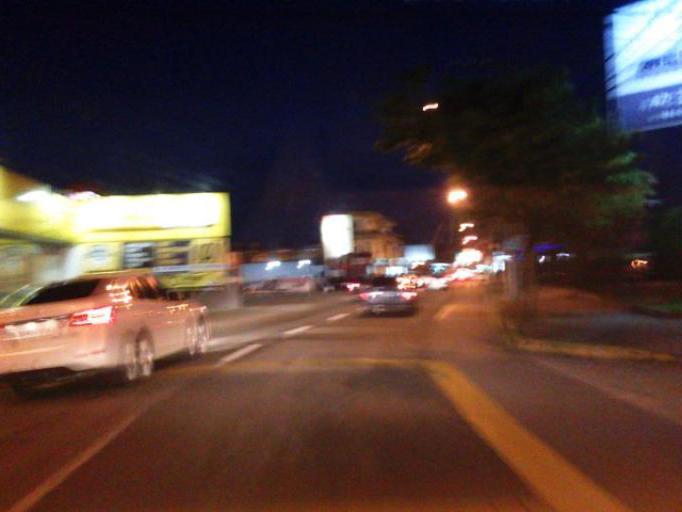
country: BR
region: Santa Catarina
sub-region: Itajai
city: Itajai
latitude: -26.8969
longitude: -48.6748
